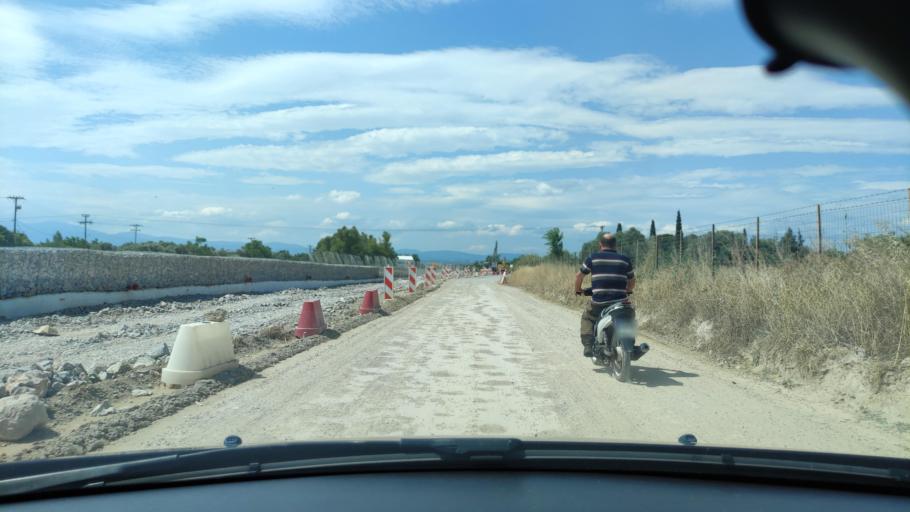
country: GR
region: Central Greece
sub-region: Nomos Evvoias
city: Vasilikon
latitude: 38.4349
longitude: 23.6648
